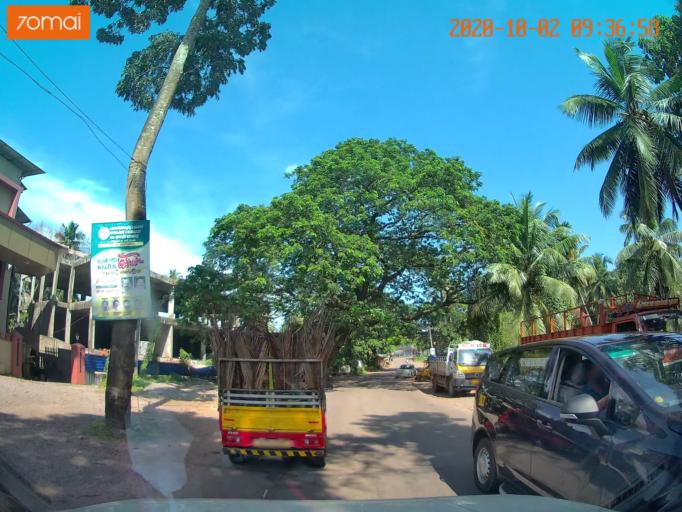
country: IN
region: Kerala
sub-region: Kozhikode
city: Nadapuram
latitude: 11.6504
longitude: 75.7544
